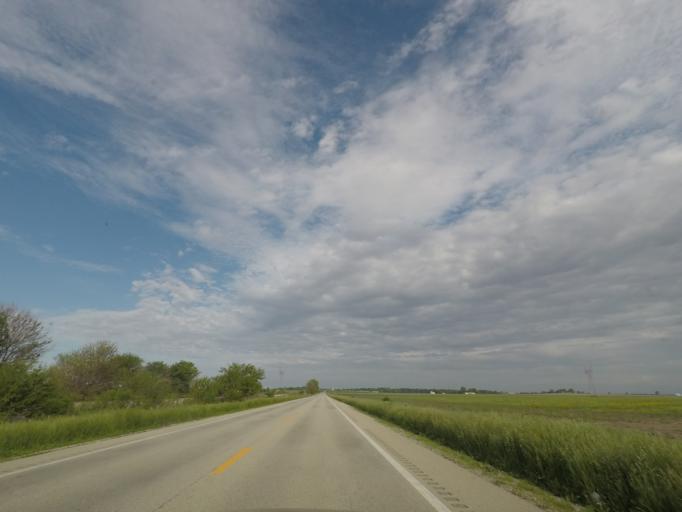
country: US
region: Illinois
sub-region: Logan County
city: Mount Pulaski
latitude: 39.9949
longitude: -89.2542
